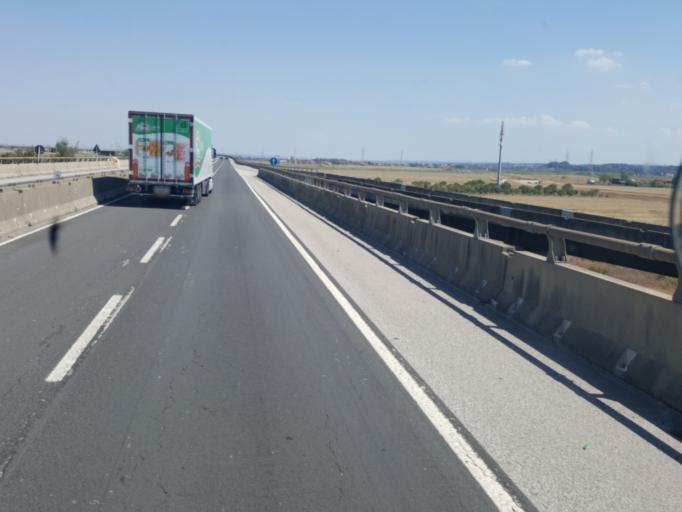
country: IT
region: Tuscany
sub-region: Provincia di Livorno
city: Guasticce
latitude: 43.6096
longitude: 10.4070
